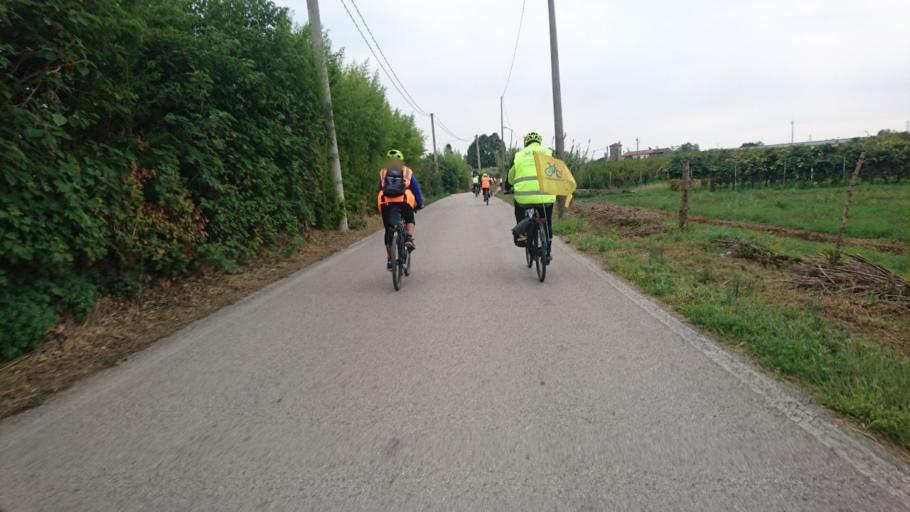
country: IT
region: Veneto
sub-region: Provincia di Verona
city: San Giovanni Lupatoto
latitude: 45.4152
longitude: 11.0573
